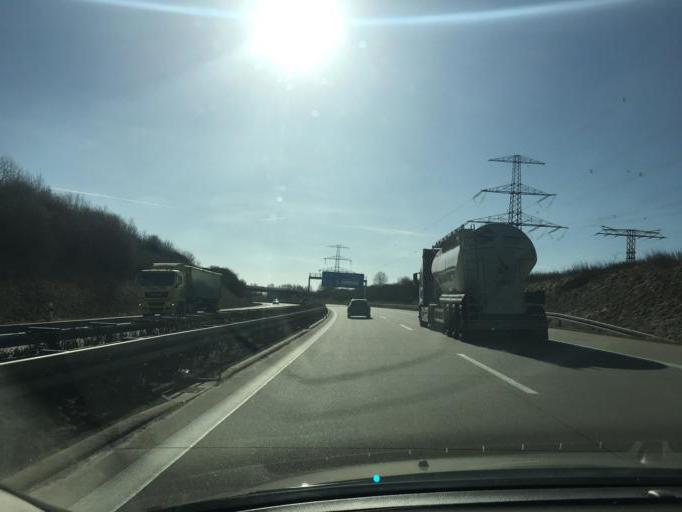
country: DE
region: Saxony
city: Hartmannsdorf
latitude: 50.8693
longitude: 12.7938
